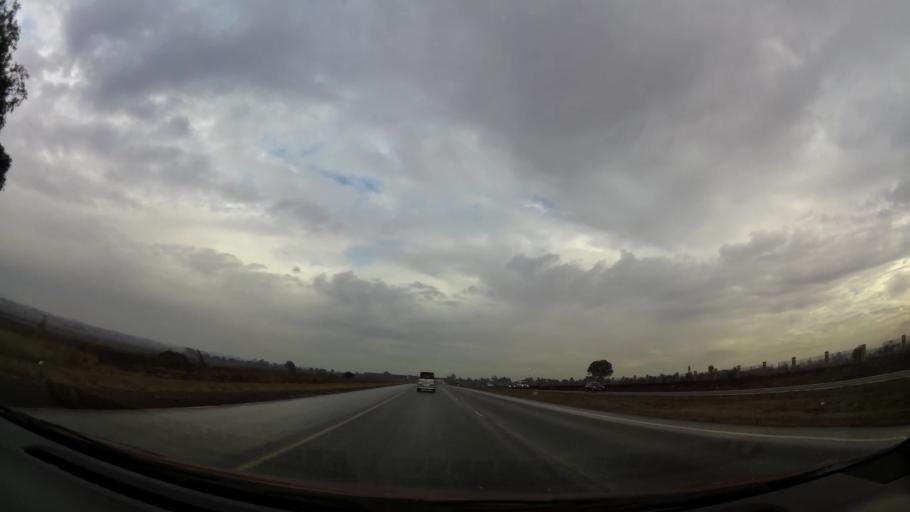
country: ZA
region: Gauteng
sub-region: City of Johannesburg Metropolitan Municipality
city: Soweto
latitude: -26.3025
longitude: 27.8599
